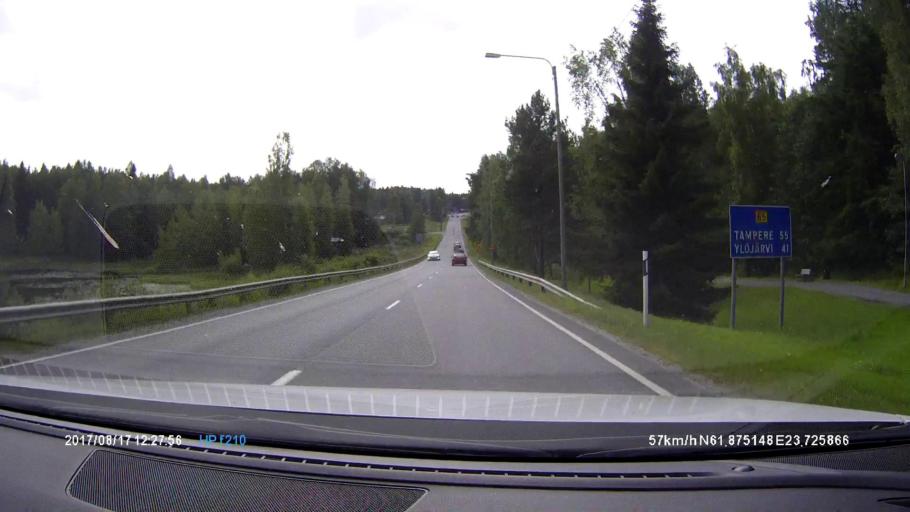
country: FI
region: Pirkanmaa
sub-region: Tampere
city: Kuru
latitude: 61.8747
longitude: 23.7260
